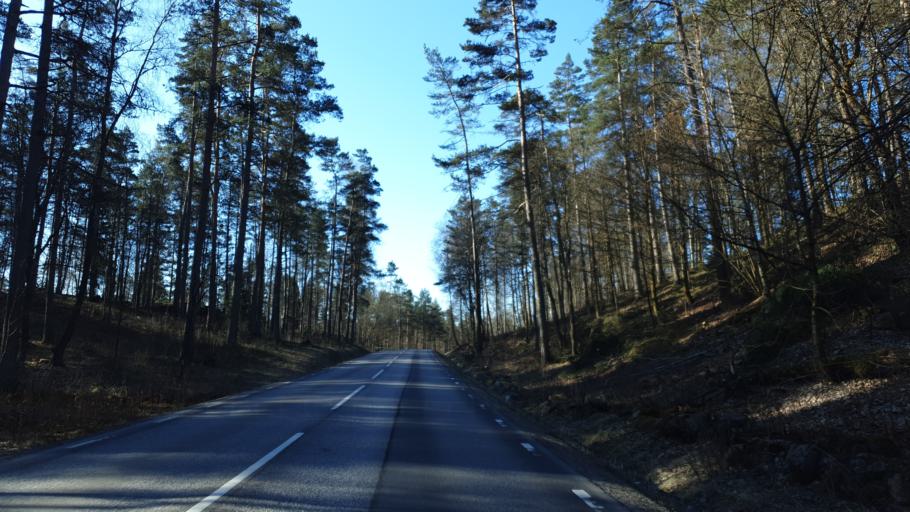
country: SE
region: Vaestra Goetaland
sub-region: Boras Kommun
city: Dalsjofors
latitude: 57.7450
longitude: 13.1067
